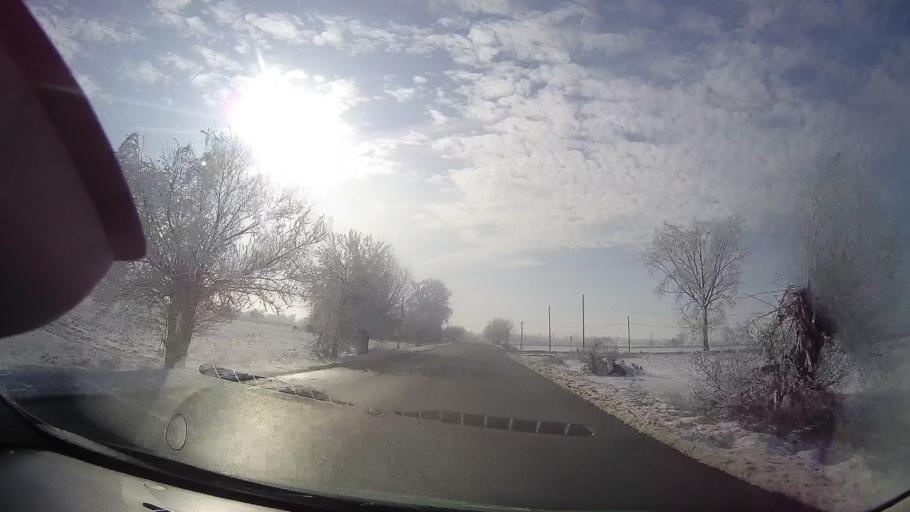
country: RO
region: Neamt
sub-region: Comuna Timisesti
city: Timisesti
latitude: 47.2416
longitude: 26.5401
